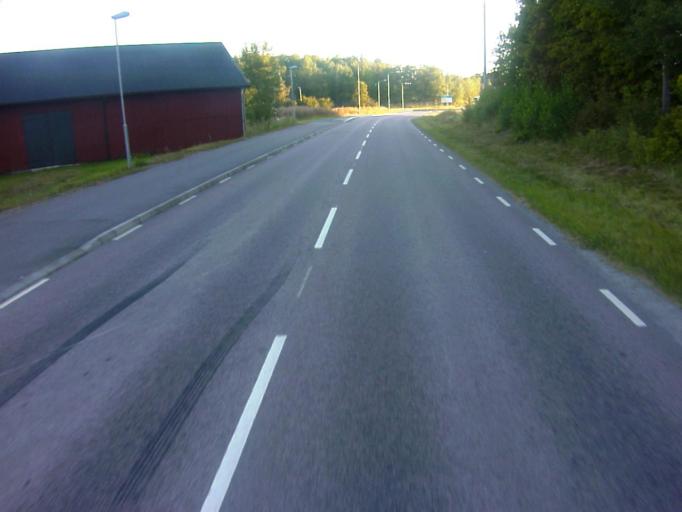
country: SE
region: Soedermanland
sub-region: Eskilstuna Kommun
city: Hallbybrunn
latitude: 59.4090
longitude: 16.4340
